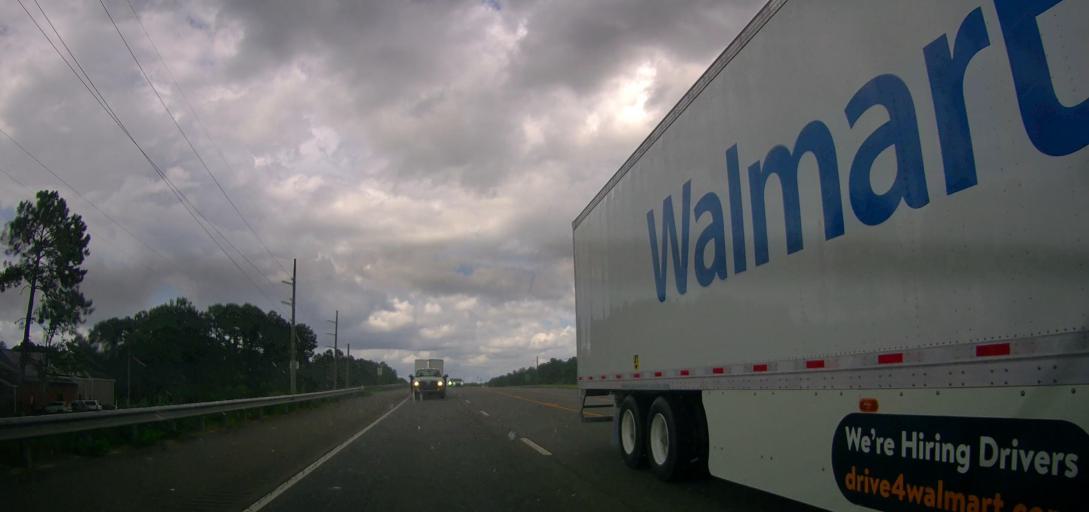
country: US
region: Georgia
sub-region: Coffee County
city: Douglas
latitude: 31.5071
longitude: -82.8739
